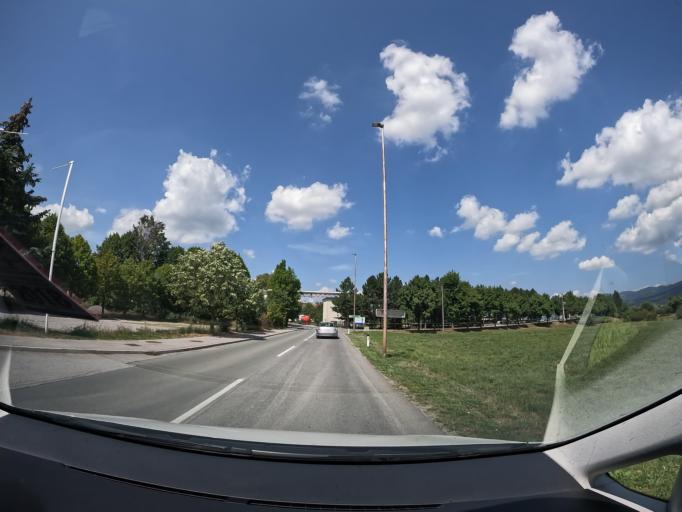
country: SI
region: Pivka
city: Pivka
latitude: 45.6795
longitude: 14.2004
